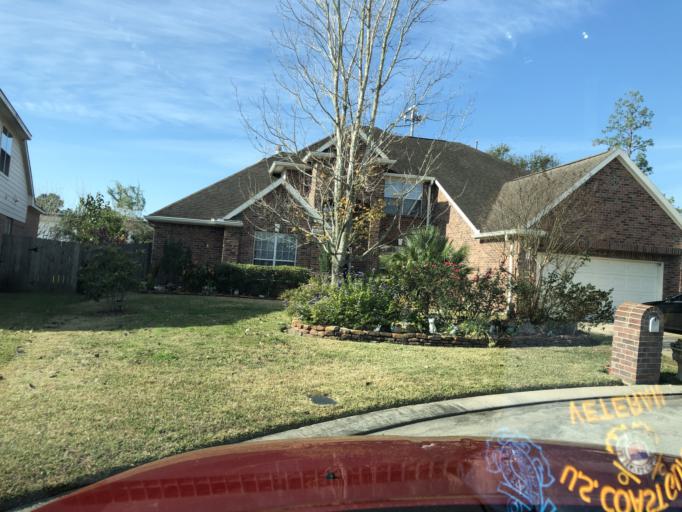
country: US
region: Texas
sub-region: Harris County
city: Tomball
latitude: 30.0256
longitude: -95.5624
